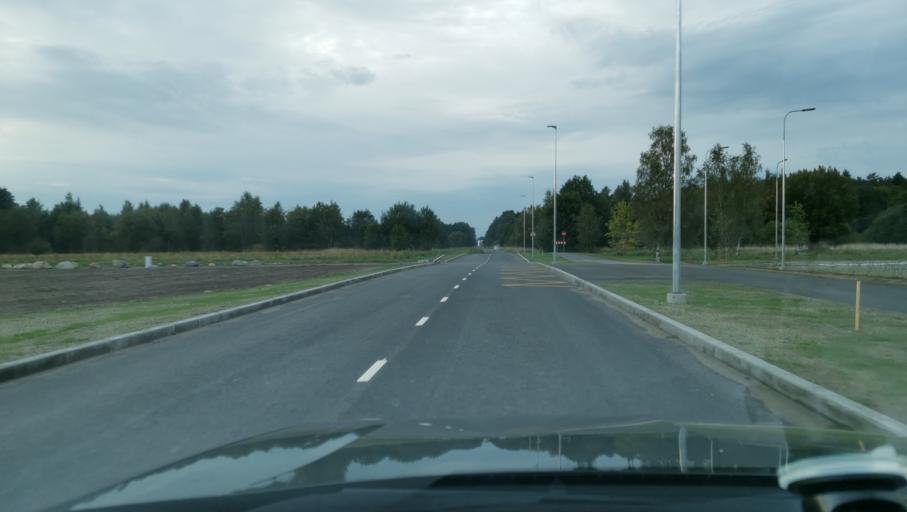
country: EE
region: Harju
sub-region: Saue vald
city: Laagri
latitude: 59.4192
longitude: 24.6303
